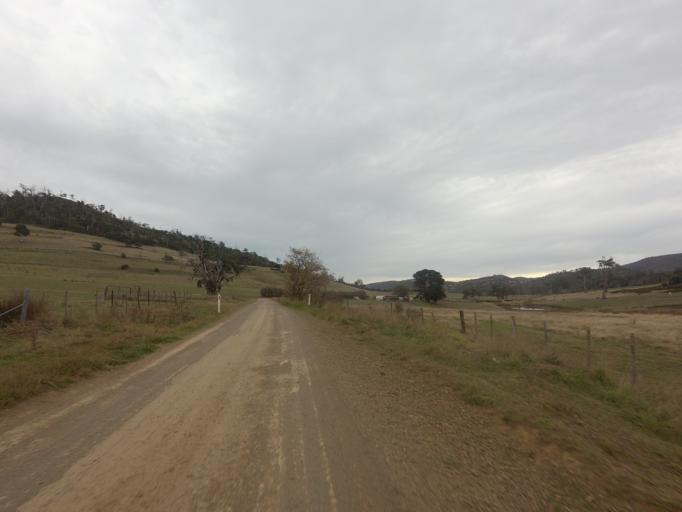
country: AU
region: Tasmania
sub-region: Derwent Valley
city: New Norfolk
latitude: -42.5527
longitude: 146.9598
